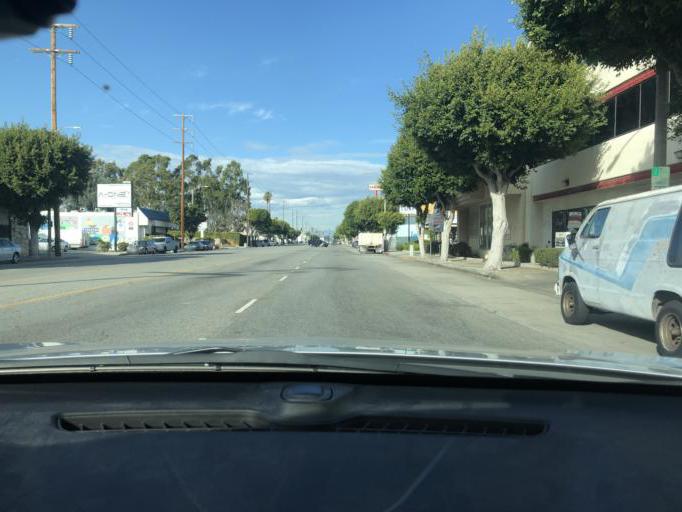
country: US
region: California
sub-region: Los Angeles County
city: Gardena
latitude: 33.8851
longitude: -118.3091
